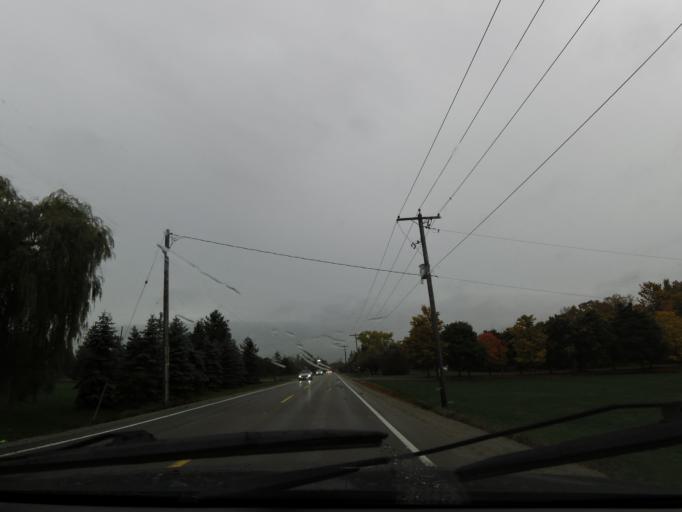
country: CA
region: Ontario
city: Burlington
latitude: 43.4449
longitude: -79.8738
